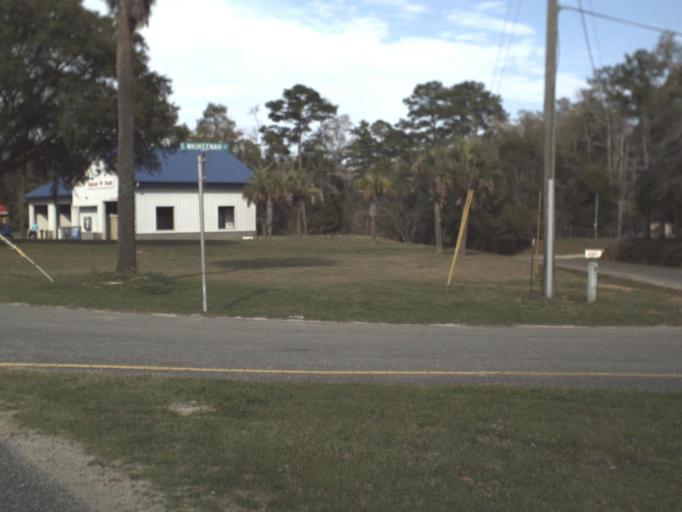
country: US
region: Florida
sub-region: Jefferson County
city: Monticello
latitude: 30.5228
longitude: -83.8730
